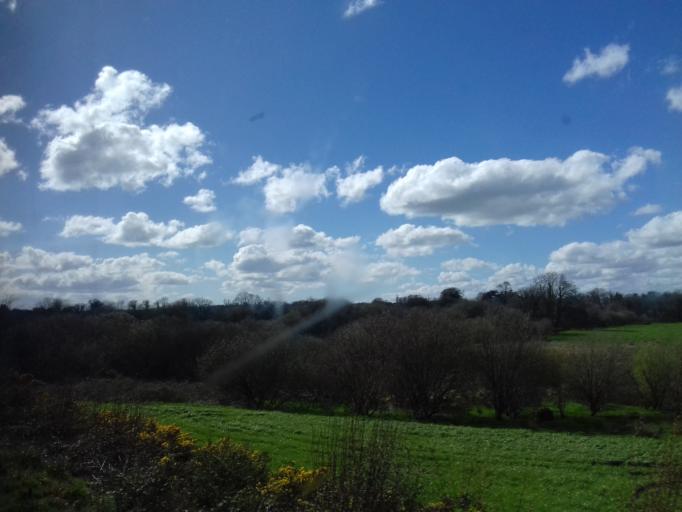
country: IE
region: Munster
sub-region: County Cork
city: Kanturk
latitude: 52.1263
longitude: -8.9086
